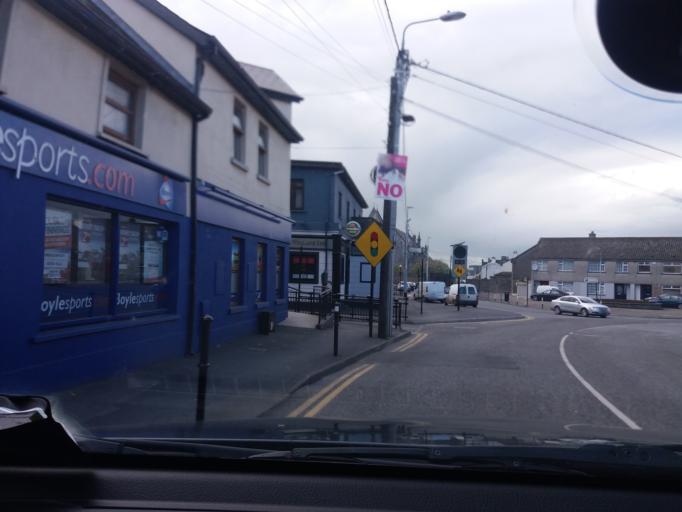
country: IE
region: Leinster
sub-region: Kilkenny
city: Kilkenny
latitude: 52.6461
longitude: -7.2507
